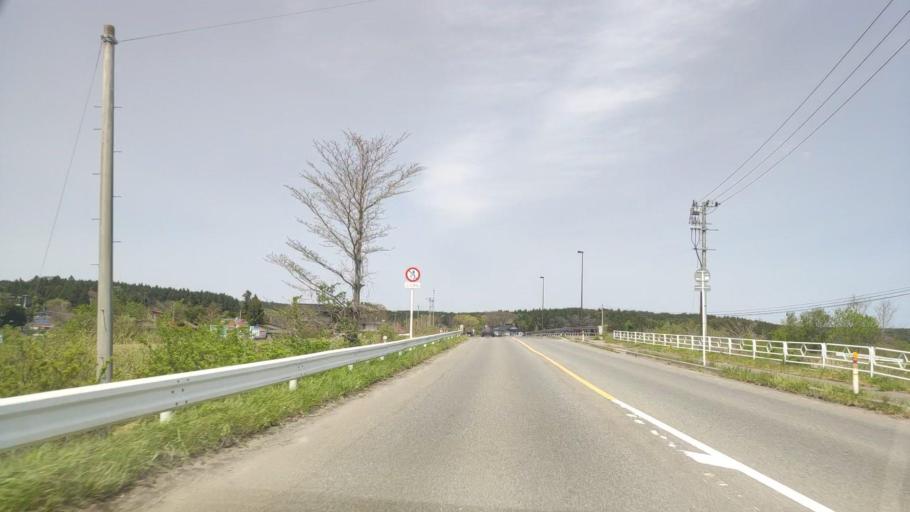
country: JP
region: Aomori
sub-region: Misawa Shi
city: Inuotose
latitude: 40.5559
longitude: 141.3886
